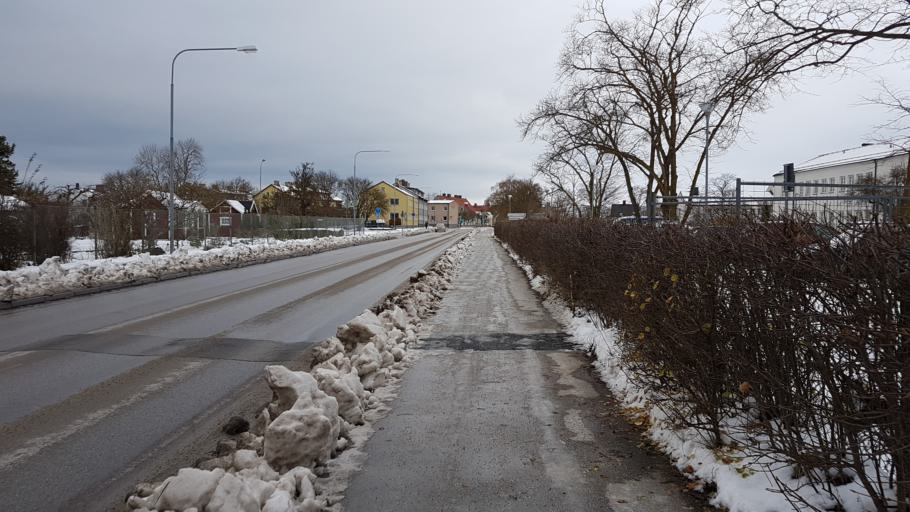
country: SE
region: Gotland
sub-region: Gotland
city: Visby
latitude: 57.6396
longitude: 18.3070
